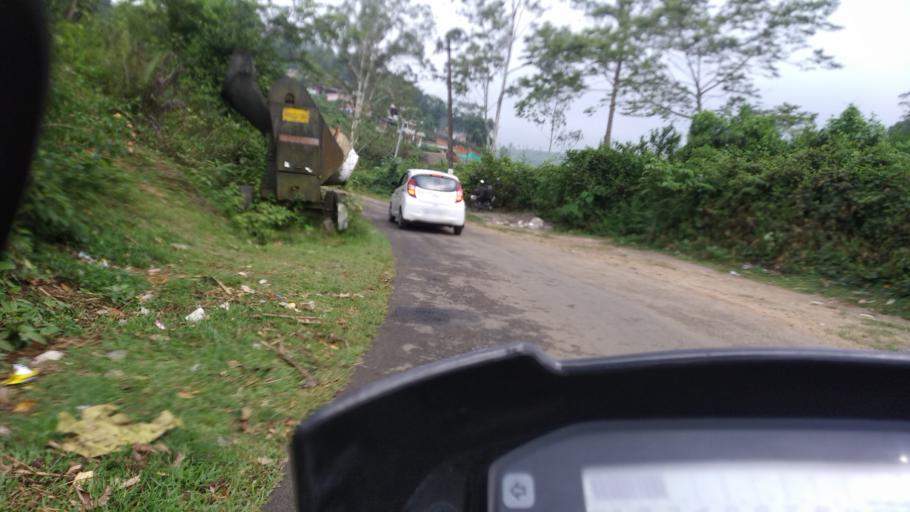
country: IN
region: Kerala
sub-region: Kottayam
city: Erattupetta
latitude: 9.5863
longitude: 77.0092
